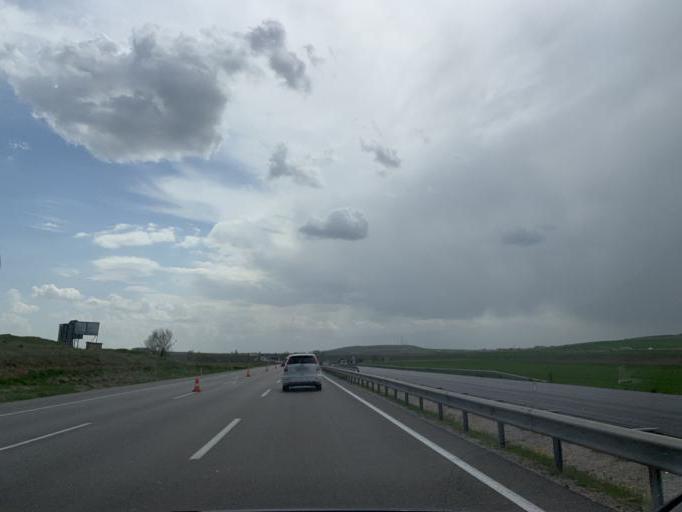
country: TR
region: Ankara
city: Polatli
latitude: 39.6339
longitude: 32.1994
